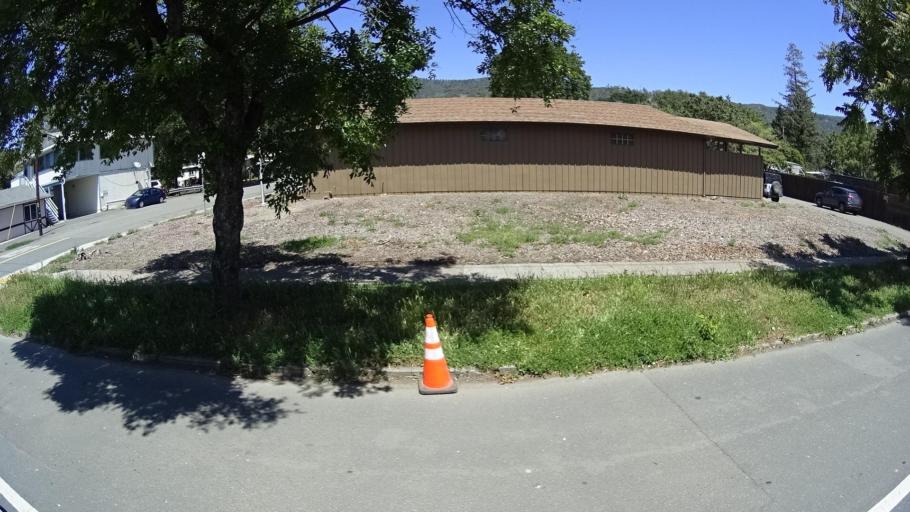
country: US
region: California
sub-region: Lake County
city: Lucerne
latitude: 39.0935
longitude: -122.7993
